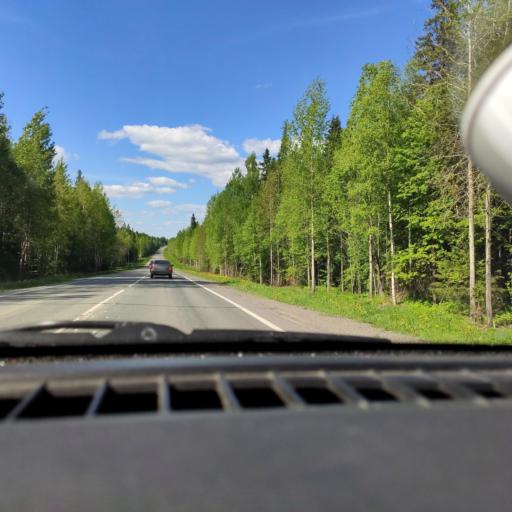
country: RU
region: Perm
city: Perm
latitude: 58.2300
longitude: 56.1624
